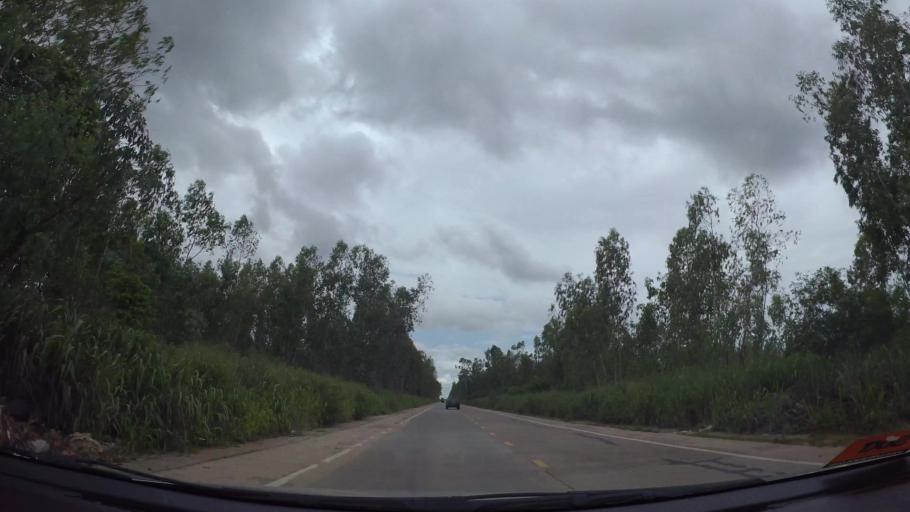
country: TH
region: Chon Buri
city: Si Racha
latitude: 13.1723
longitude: 100.9841
